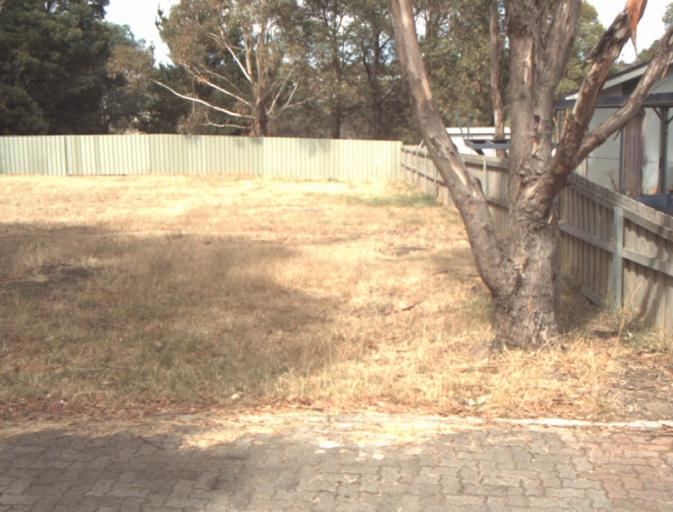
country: AU
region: Tasmania
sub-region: Launceston
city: Summerhill
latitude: -41.4589
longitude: 147.1239
